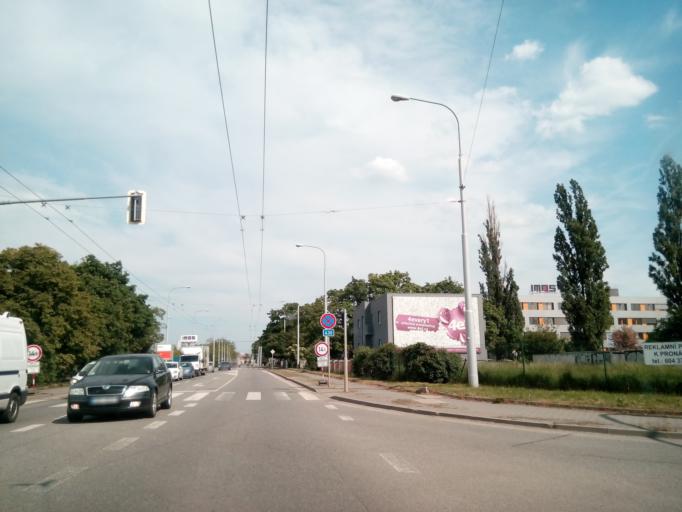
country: CZ
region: South Moravian
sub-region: Mesto Brno
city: Brno
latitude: 49.1853
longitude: 16.6575
